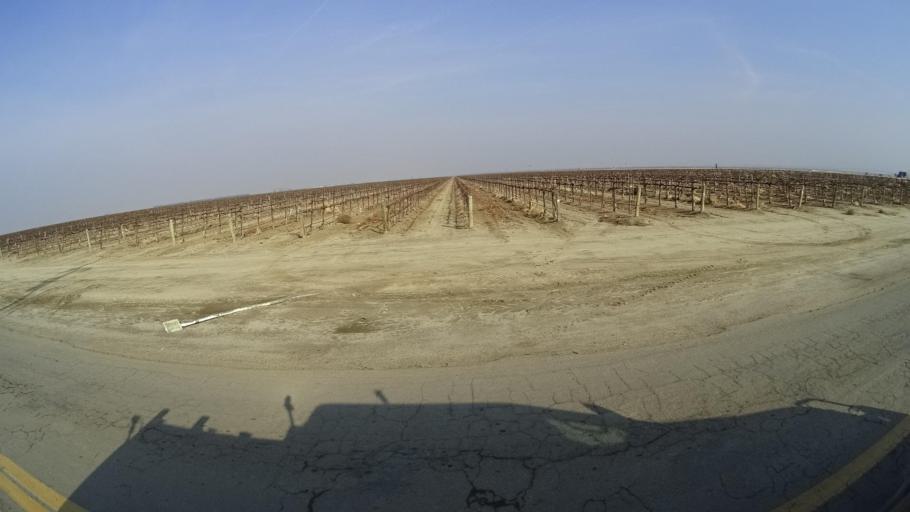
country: US
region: California
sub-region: Kern County
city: Lebec
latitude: 34.9931
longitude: -118.9012
